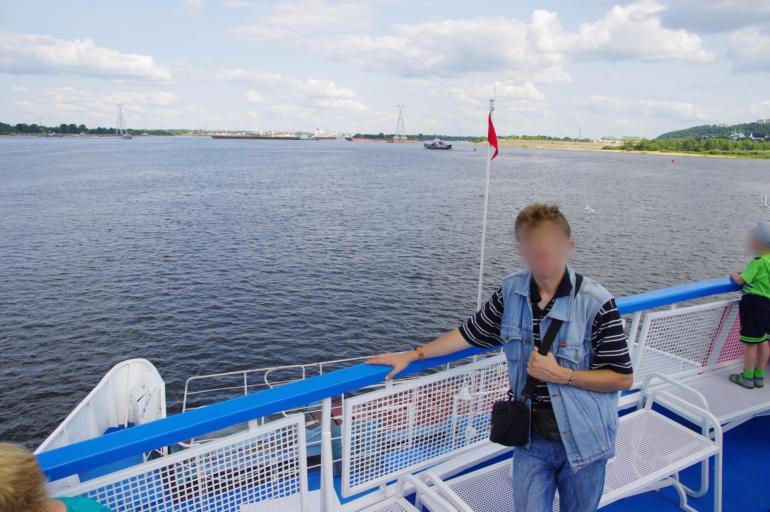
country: RU
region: Nizjnij Novgorod
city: Nizhniy Novgorod
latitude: 56.3357
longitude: 44.0210
